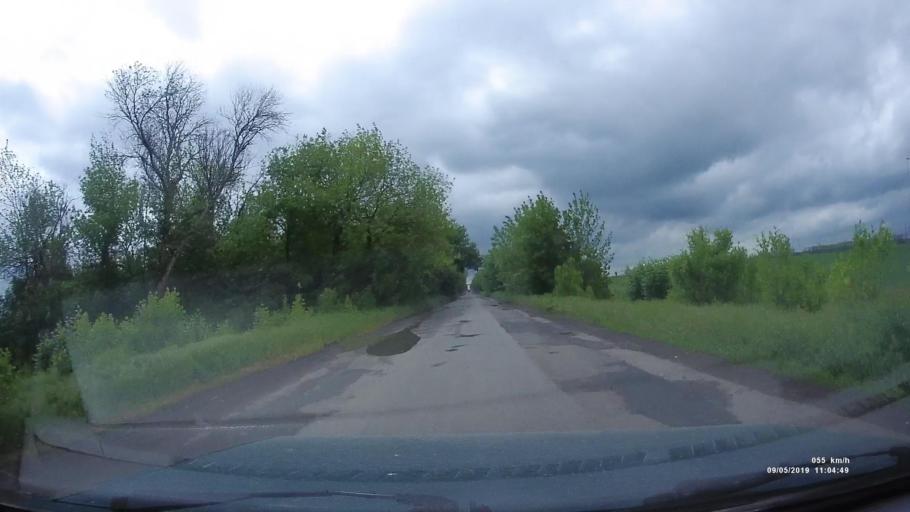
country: RU
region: Krasnodarskiy
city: Kanelovskaya
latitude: 46.8132
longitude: 39.2099
